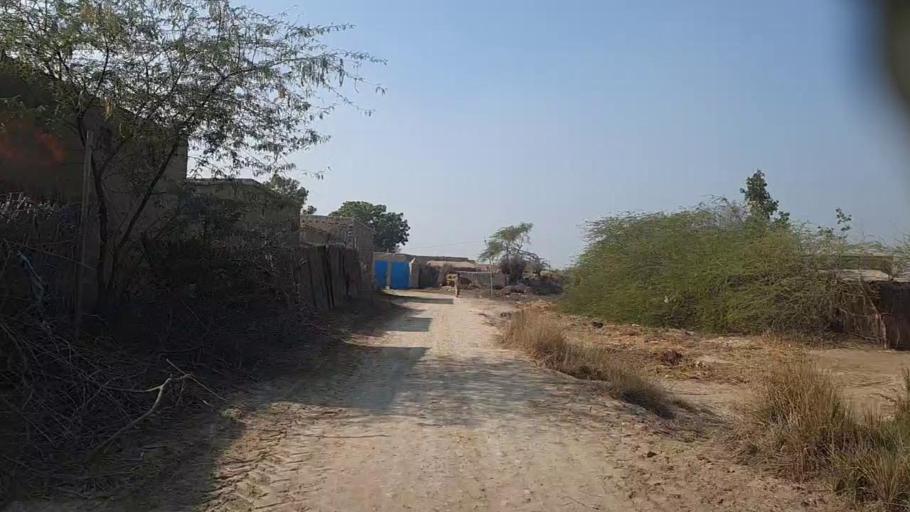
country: PK
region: Sindh
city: Khairpur
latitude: 27.9302
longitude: 69.6664
